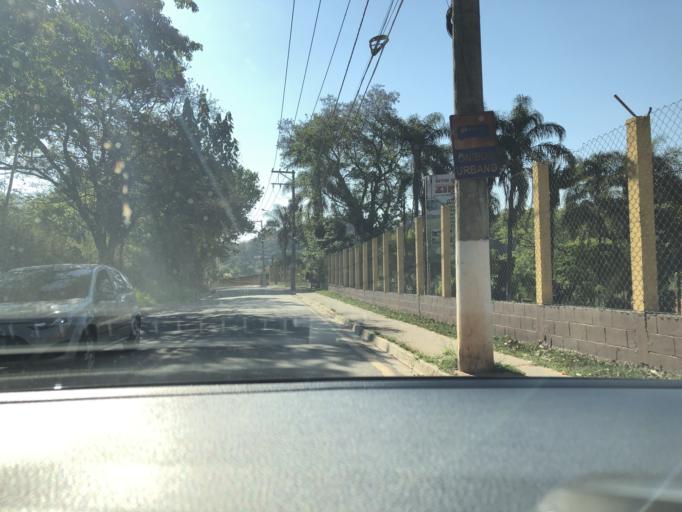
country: BR
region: Sao Paulo
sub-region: Campo Limpo Paulista
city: Campo Limpo Paulista
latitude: -23.1855
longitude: -46.7976
